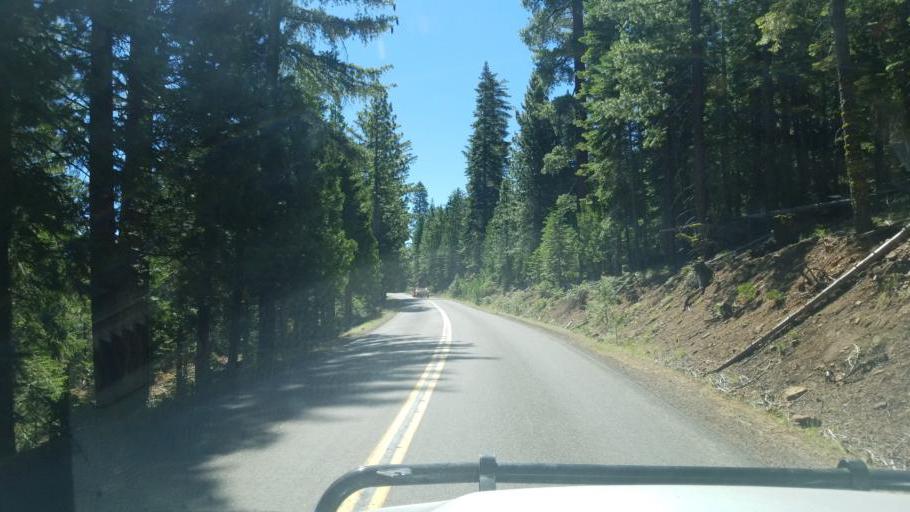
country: US
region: California
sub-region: Lassen County
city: Susanville
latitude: 40.5094
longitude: -120.7674
